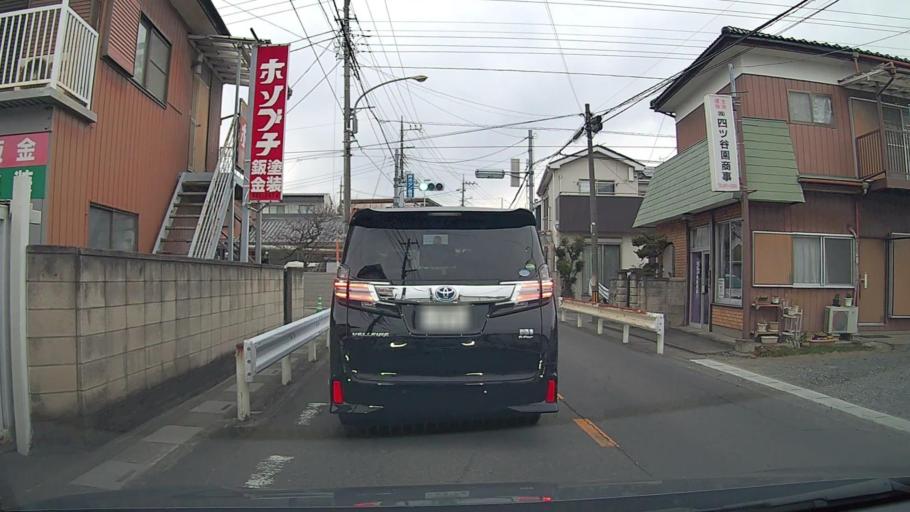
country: JP
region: Saitama
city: Yono
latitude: 35.8402
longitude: 139.6386
